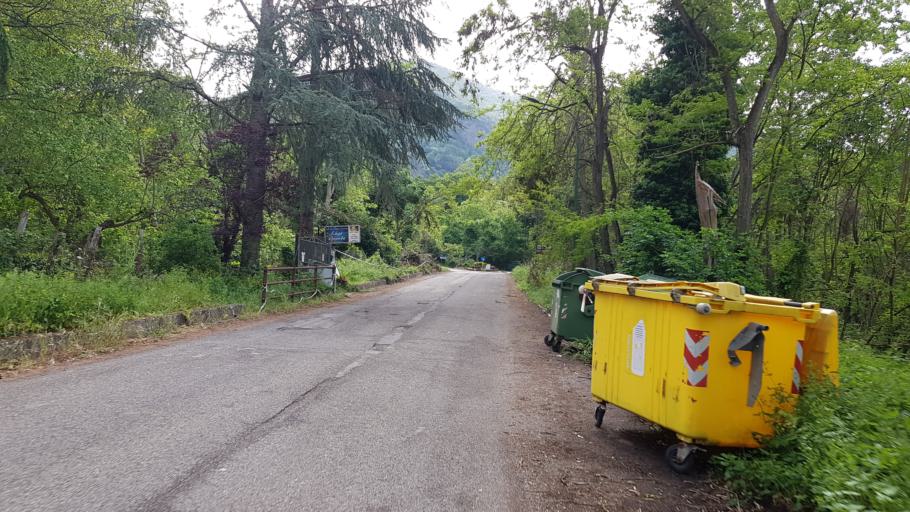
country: IT
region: Basilicate
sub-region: Provincia di Potenza
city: Barile
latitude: 40.9370
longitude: 15.6061
